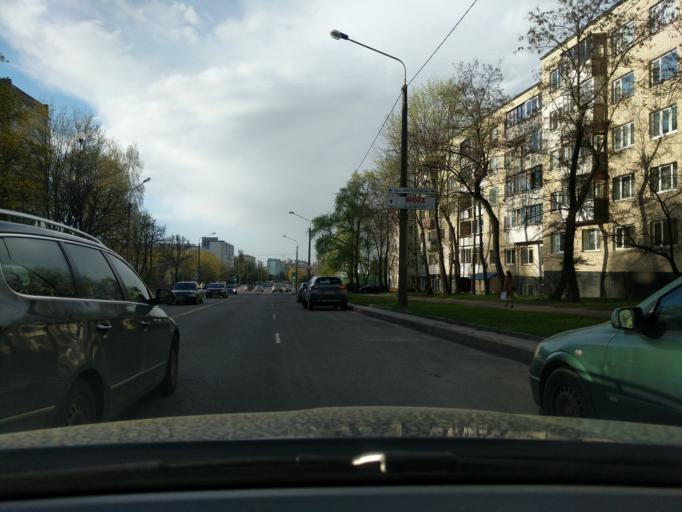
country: BY
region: Minsk
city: Novoye Medvezhino
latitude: 53.9139
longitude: 27.4800
